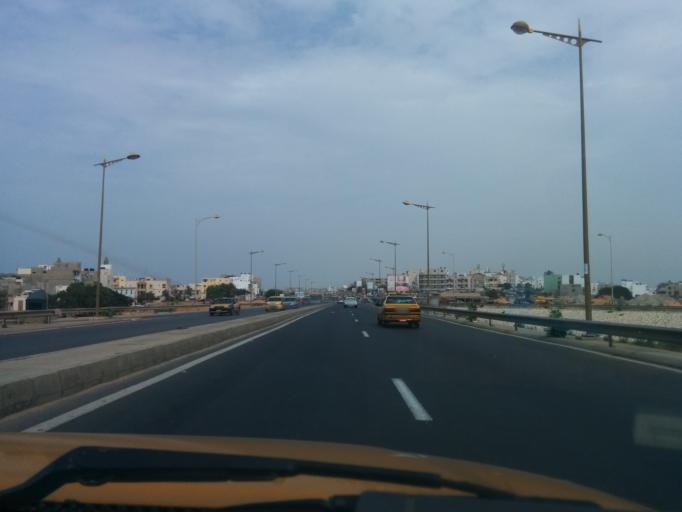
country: SN
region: Dakar
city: Grand Dakar
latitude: 14.7485
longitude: -17.4617
